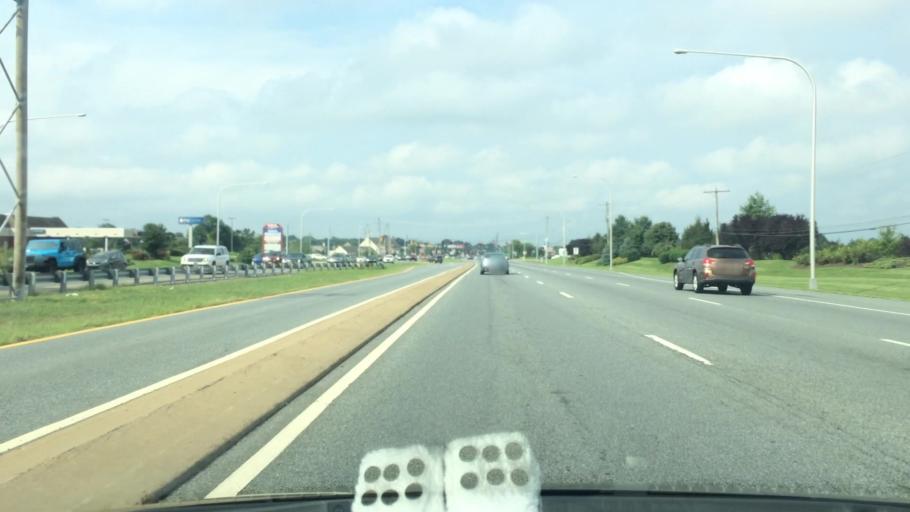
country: US
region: Delaware
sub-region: New Castle County
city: Bear
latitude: 39.6351
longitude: -75.6563
